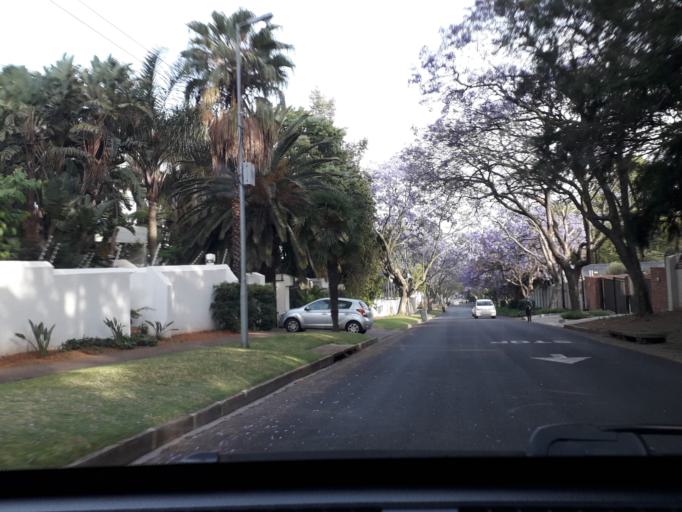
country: ZA
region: Gauteng
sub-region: City of Johannesburg Metropolitan Municipality
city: Johannesburg
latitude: -26.1375
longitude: 28.0810
